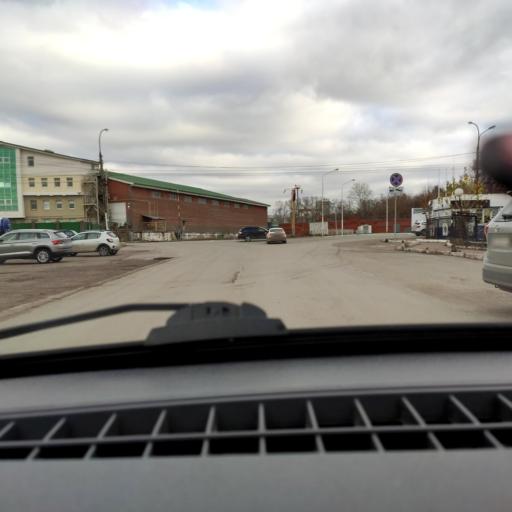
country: RU
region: Bashkortostan
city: Ufa
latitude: 54.8035
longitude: 56.0959
